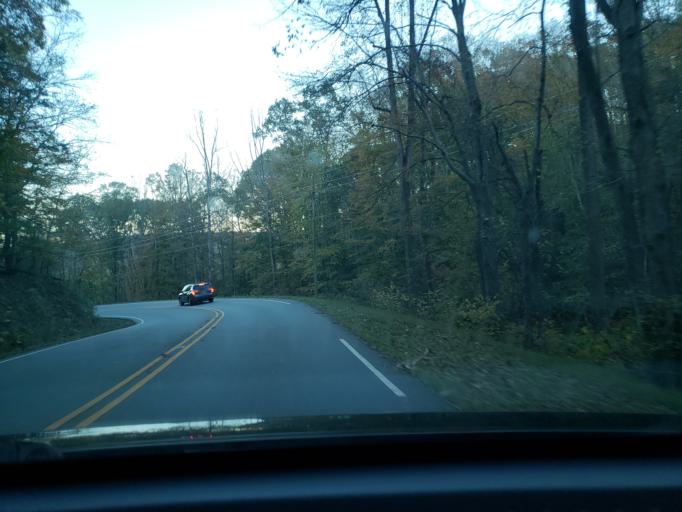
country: US
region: North Carolina
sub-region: Stokes County
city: Danbury
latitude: 36.4032
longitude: -80.2023
